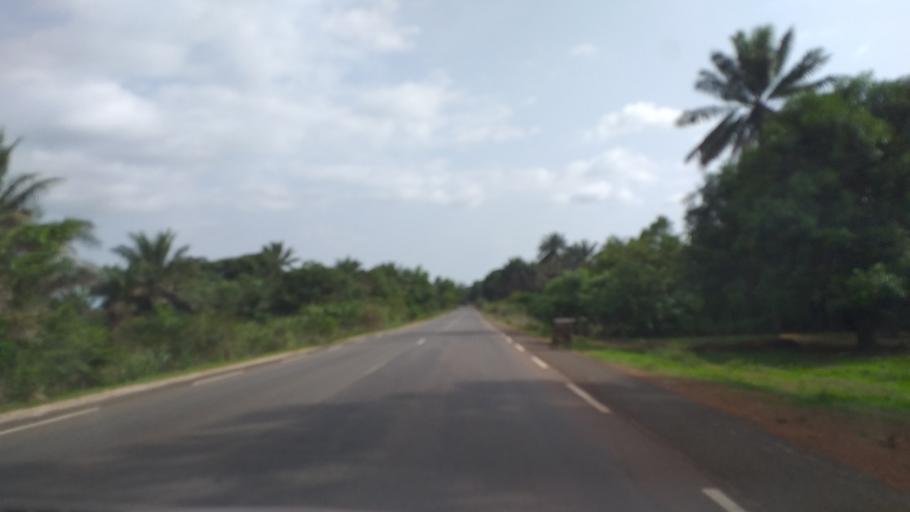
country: GN
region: Boke
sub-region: Boke Prefecture
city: Sangueya
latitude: 10.5705
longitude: -14.3975
